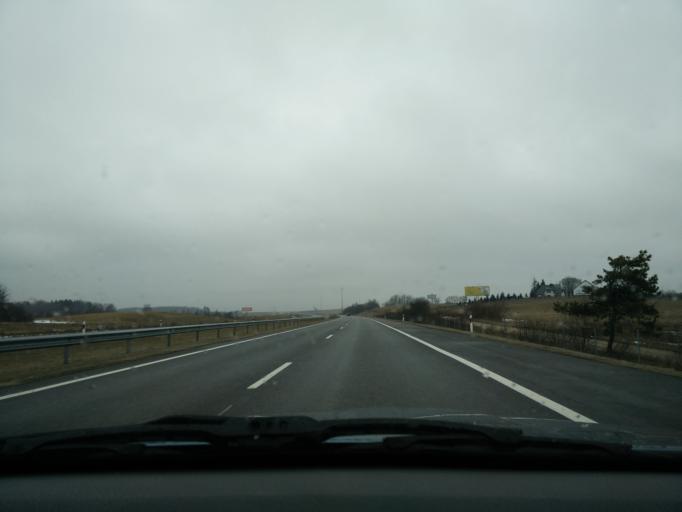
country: LT
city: Silale
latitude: 55.5544
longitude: 22.2543
